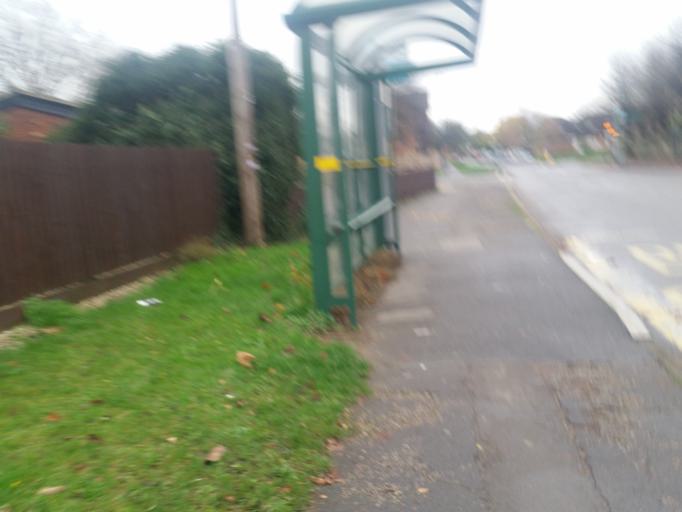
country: GB
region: England
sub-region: Derbyshire
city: Borrowash
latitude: 52.8947
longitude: -1.4182
